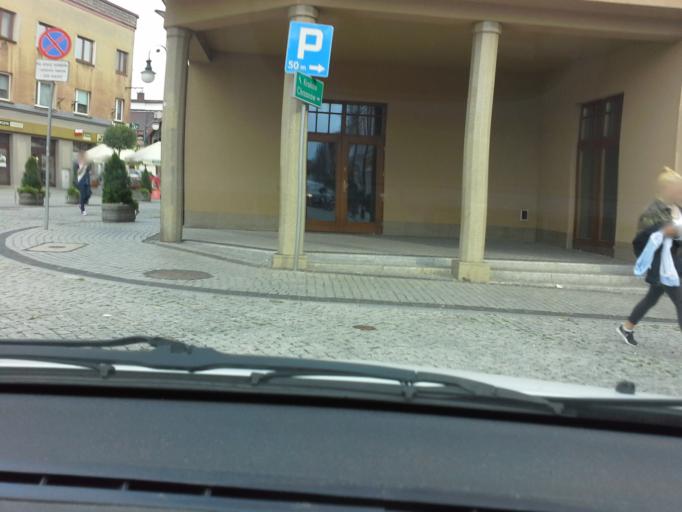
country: PL
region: Lesser Poland Voivodeship
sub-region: Powiat chrzanowski
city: Trzebinia
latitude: 50.1594
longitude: 19.4716
